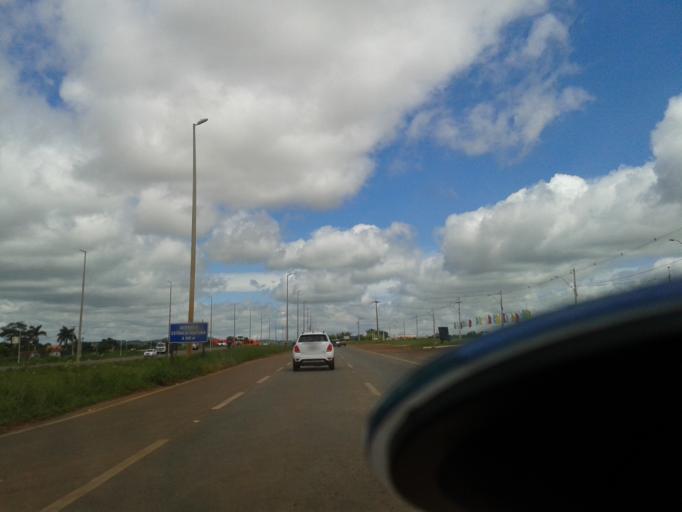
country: BR
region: Goias
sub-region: Goianira
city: Goianira
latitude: -16.5298
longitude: -49.4093
